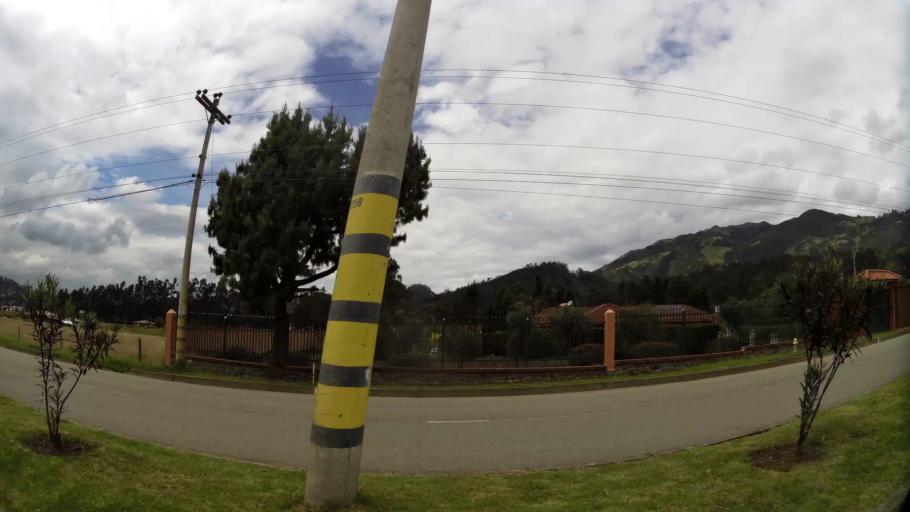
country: EC
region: Azuay
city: Cuenca
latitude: -2.8900
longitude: -79.0610
